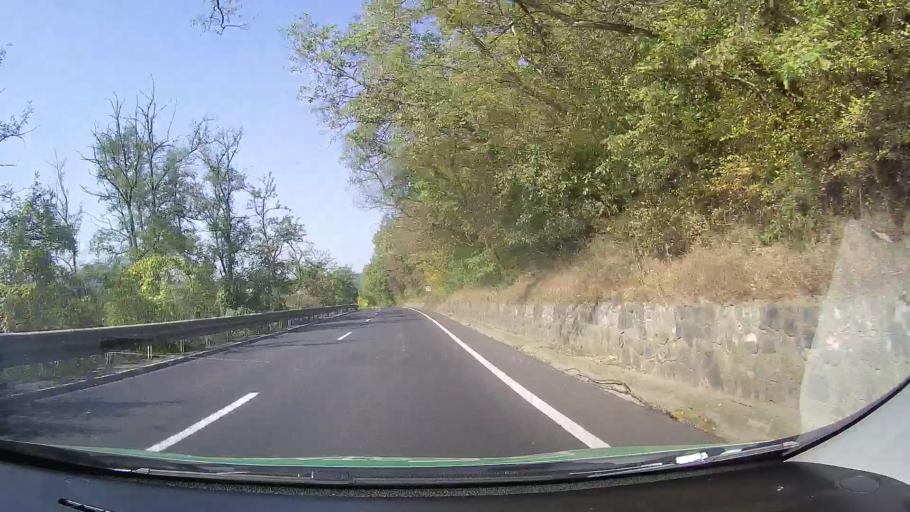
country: RO
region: Hunedoara
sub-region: Comuna Burjuc
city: Burjuc
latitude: 45.9414
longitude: 22.5184
